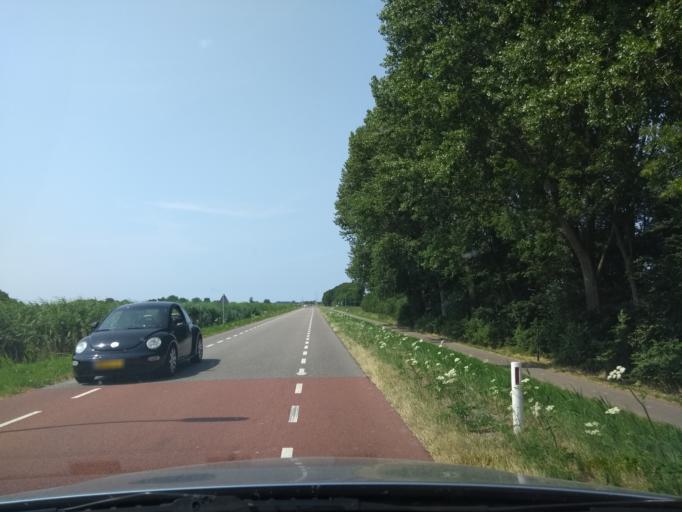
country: NL
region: North Holland
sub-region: Gemeente Langedijk
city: Broek op Langedijk
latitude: 52.6340
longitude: 4.8198
